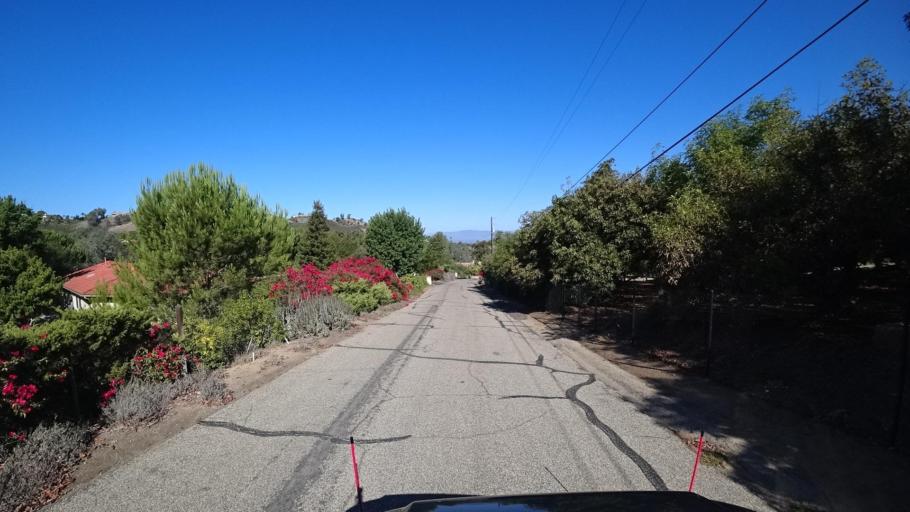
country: US
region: California
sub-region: San Diego County
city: Hidden Meadows
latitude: 33.2305
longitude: -117.1119
